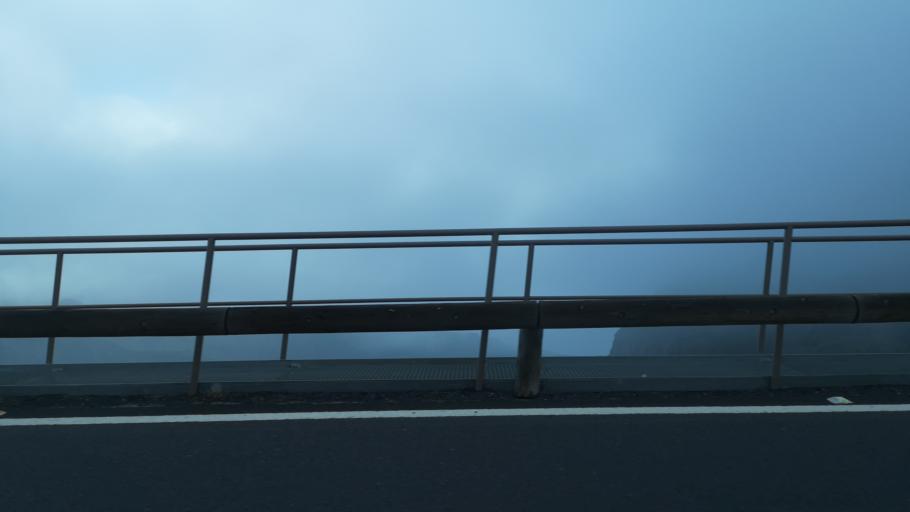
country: ES
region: Canary Islands
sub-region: Provincia de Santa Cruz de Tenerife
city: Alajero
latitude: 28.1045
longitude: -17.2095
